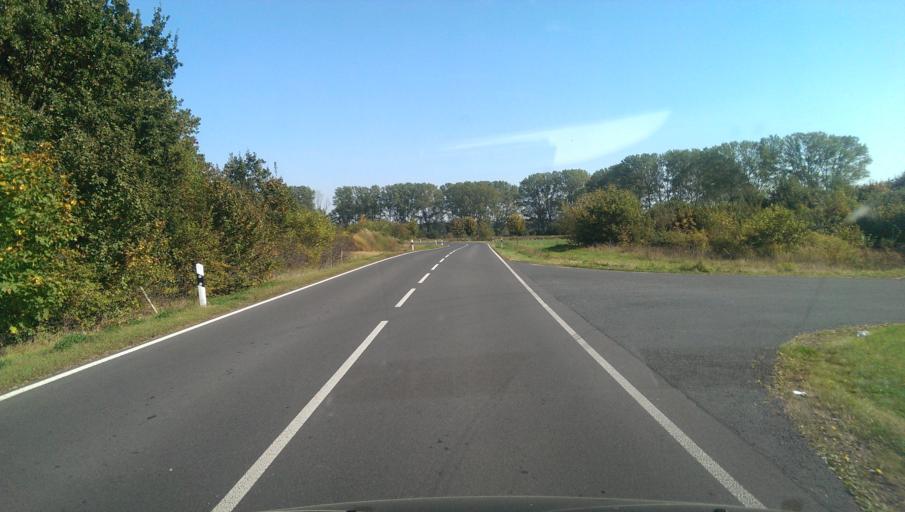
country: DE
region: Brandenburg
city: Trebbin
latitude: 52.2467
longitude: 13.2629
